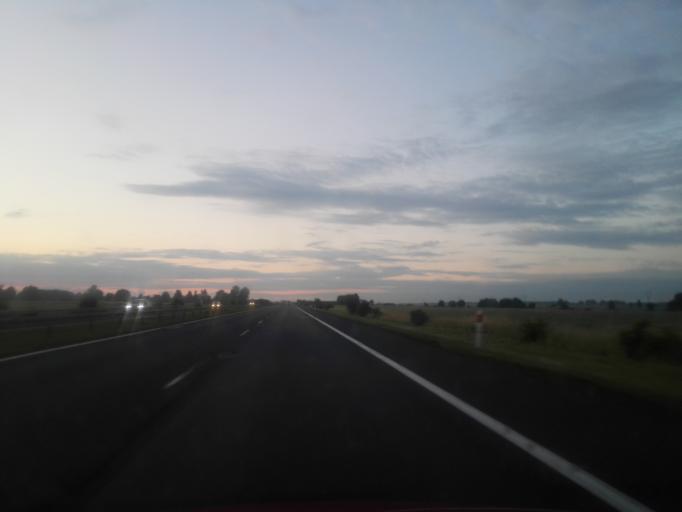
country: PL
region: Lodz Voivodeship
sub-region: Powiat radomszczanski
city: Kamiensk
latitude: 51.2588
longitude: 19.5286
